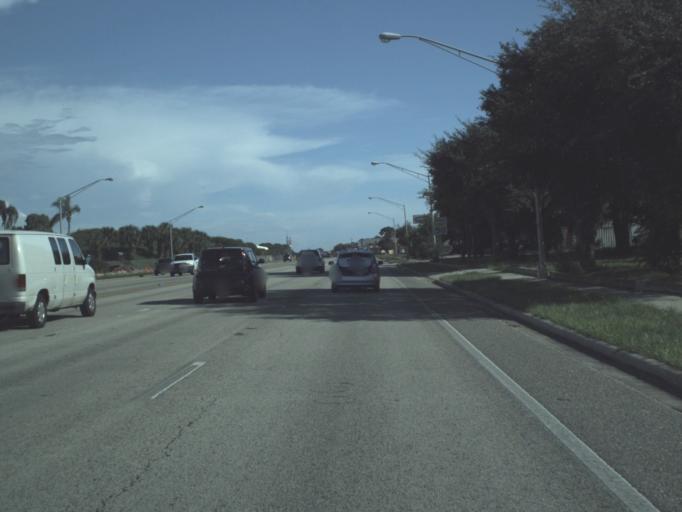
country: US
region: Florida
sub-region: Manatee County
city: Whitfield
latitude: 27.4067
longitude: -82.5691
